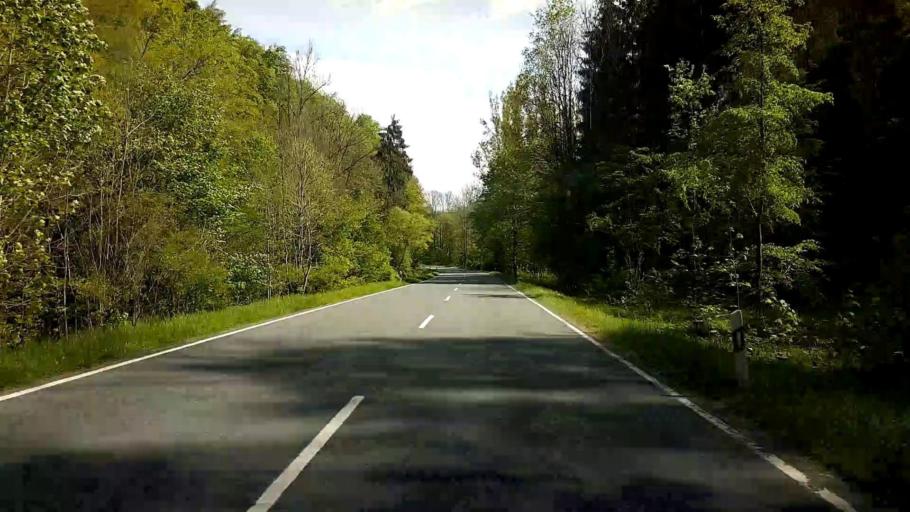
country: DE
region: Bavaria
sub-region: Upper Franconia
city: Ebermannstadt
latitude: 49.8020
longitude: 11.1675
